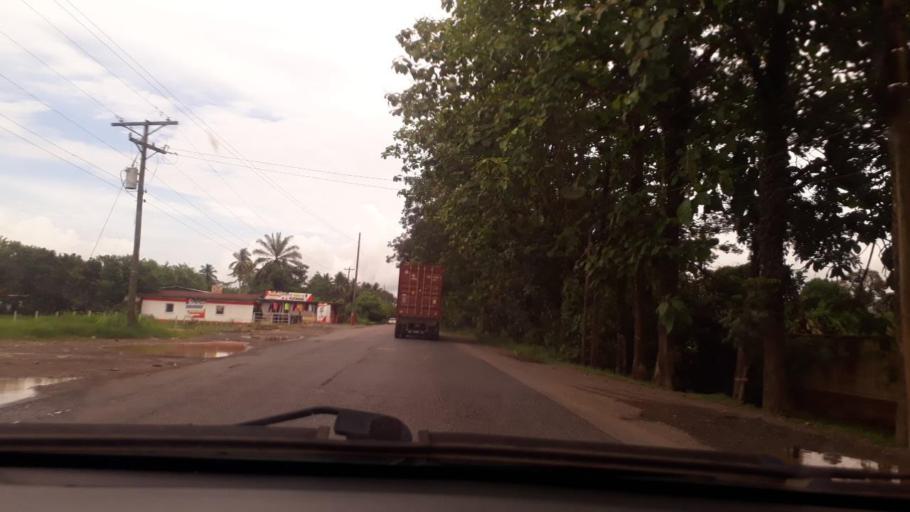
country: GT
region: Izabal
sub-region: Municipio de Puerto Barrios
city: Puerto Barrios
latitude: 15.5829
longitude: -88.5938
